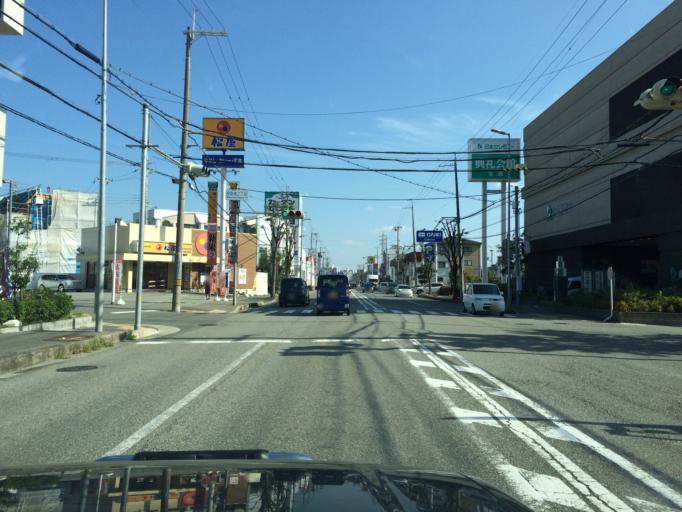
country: JP
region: Hyogo
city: Takarazuka
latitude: 34.7957
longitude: 135.3739
